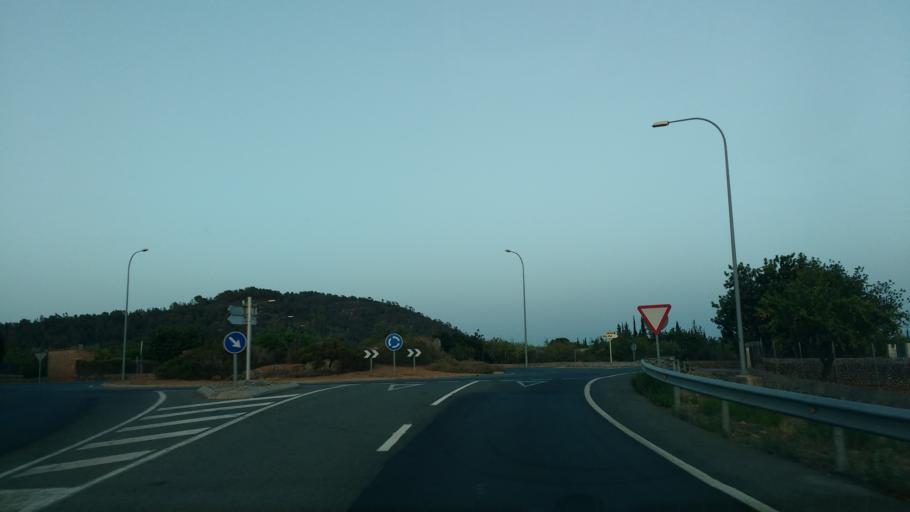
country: ES
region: Balearic Islands
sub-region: Illes Balears
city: Bunyola
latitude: 39.6676
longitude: 2.7046
